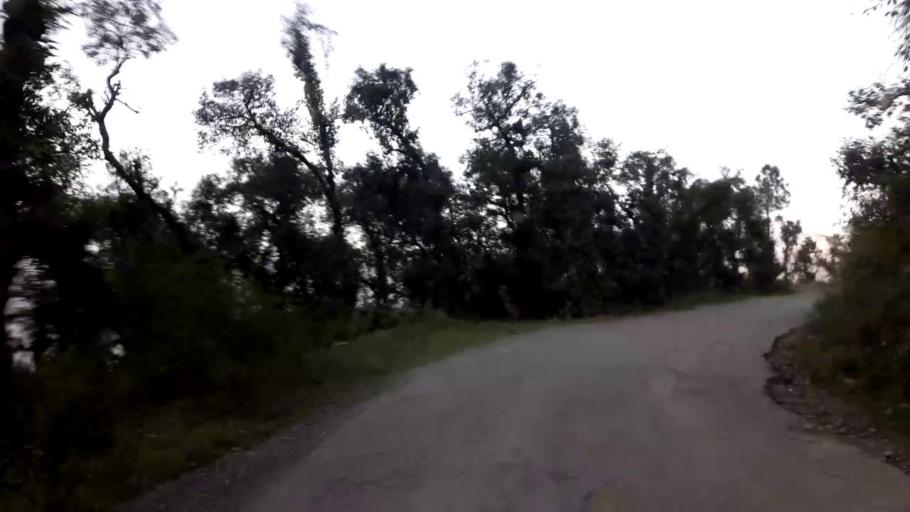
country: IN
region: Himachal Pradesh
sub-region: Shimla
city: Shimla
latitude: 31.0591
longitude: 77.1539
